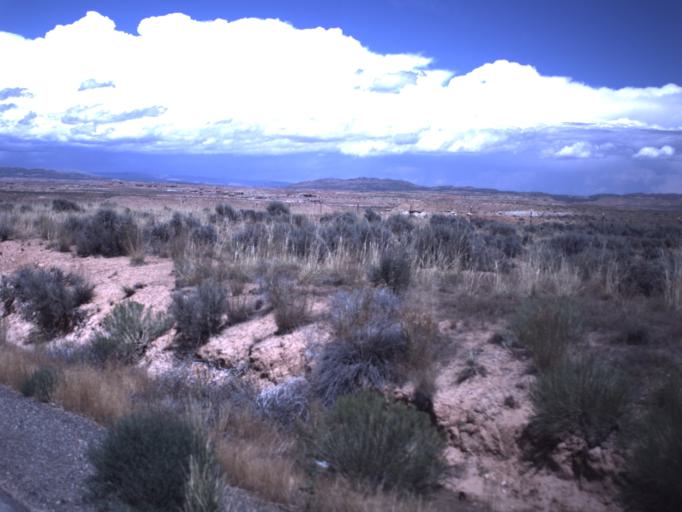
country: US
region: Utah
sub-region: Uintah County
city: Maeser
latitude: 40.3126
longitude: -109.6916
